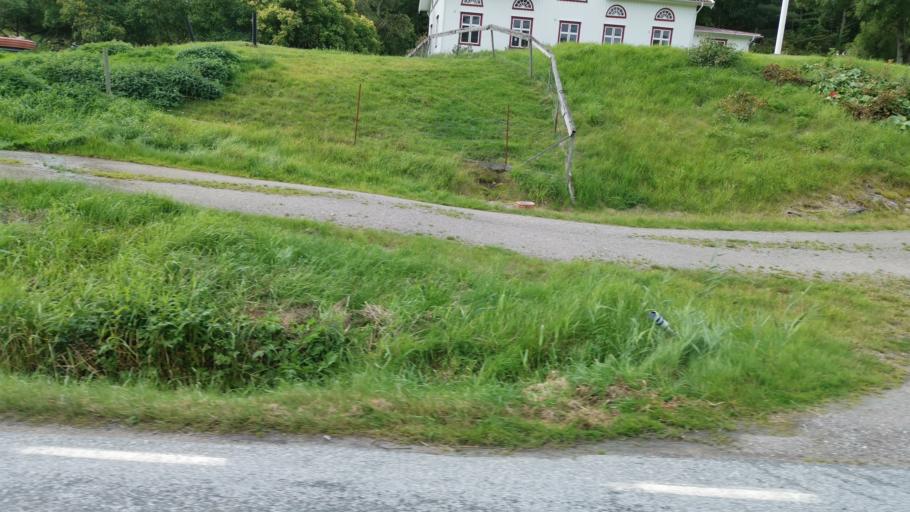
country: SE
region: Vaestra Goetaland
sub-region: Tjorns Kommun
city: Myggenas
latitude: 58.0403
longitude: 11.6511
